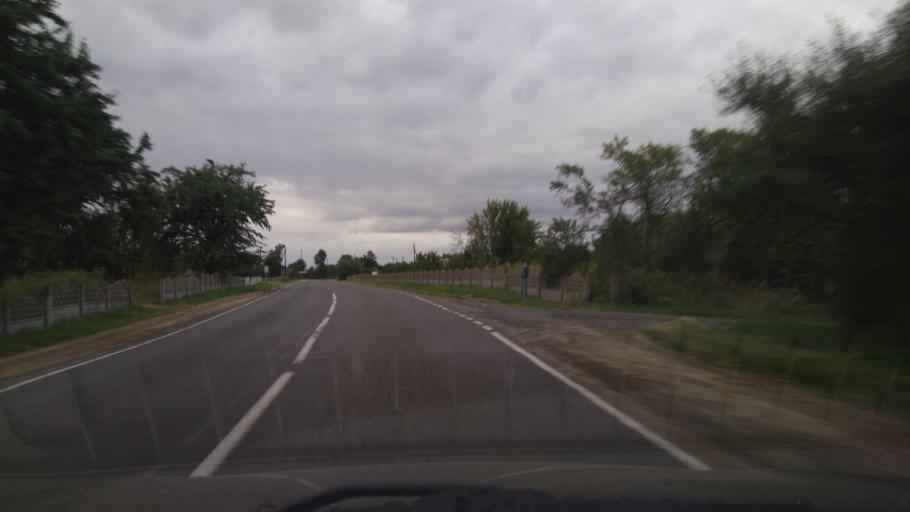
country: BY
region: Brest
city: Byaroza
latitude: 52.4202
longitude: 24.9807
